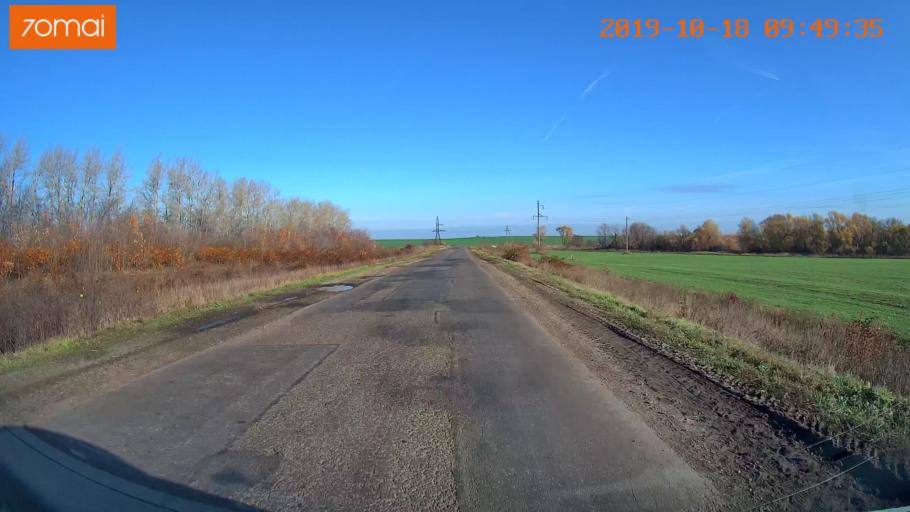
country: RU
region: Tula
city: Kazachka
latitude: 53.3196
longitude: 38.2684
